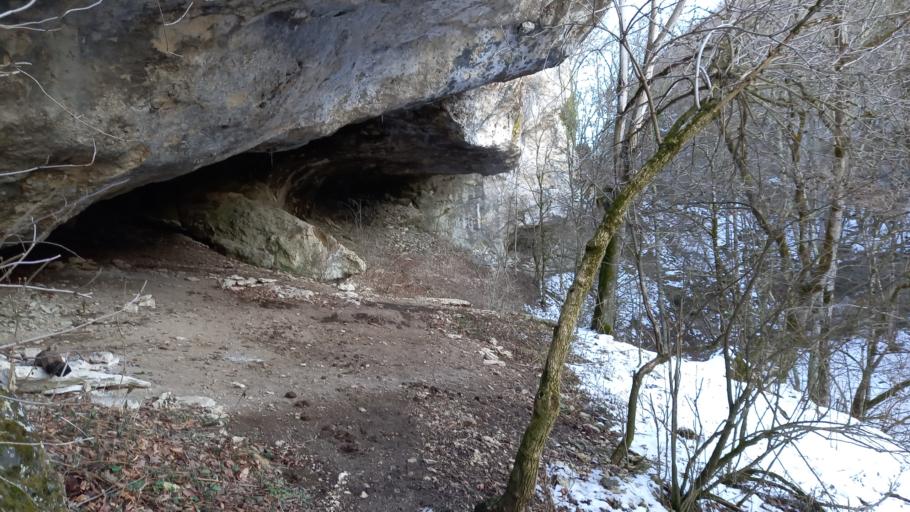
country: RU
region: Adygeya
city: Kamennomostskiy
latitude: 44.2807
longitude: 40.3501
